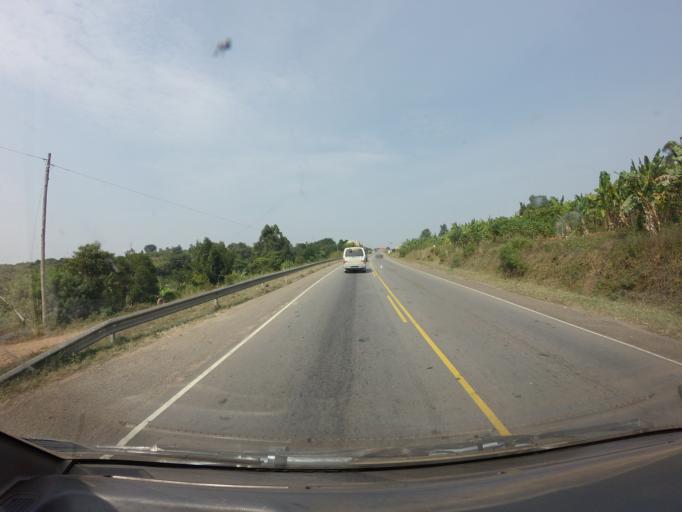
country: UG
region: Central Region
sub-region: Lwengo District
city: Lwengo
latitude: -0.3981
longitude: 31.4009
